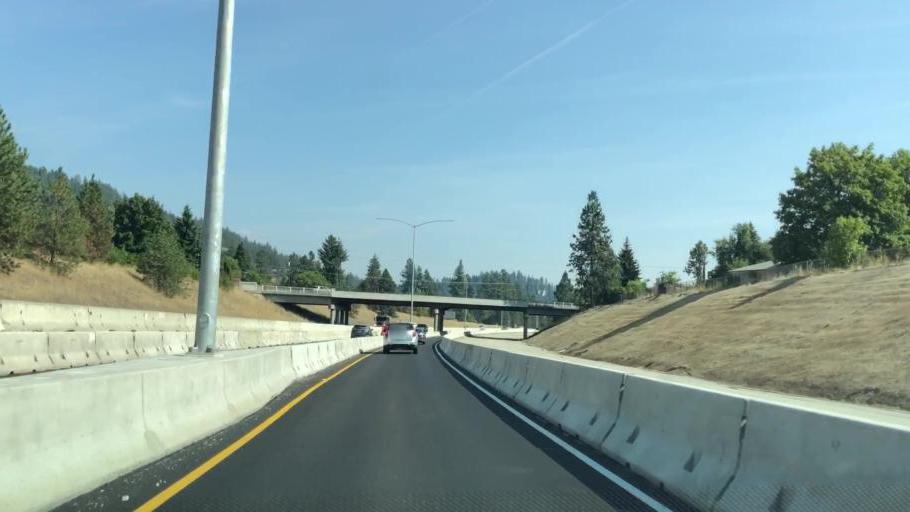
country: US
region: Idaho
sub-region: Kootenai County
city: Coeur d'Alene
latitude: 47.6963
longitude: -116.7748
